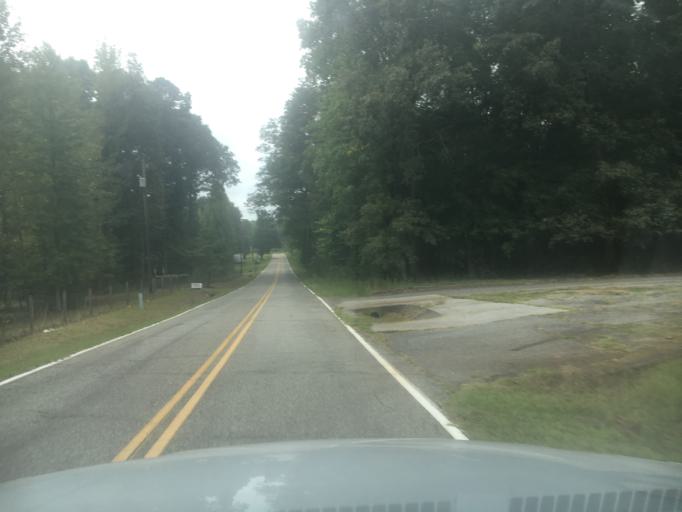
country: US
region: South Carolina
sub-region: Spartanburg County
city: Inman
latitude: 35.1821
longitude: -82.0467
